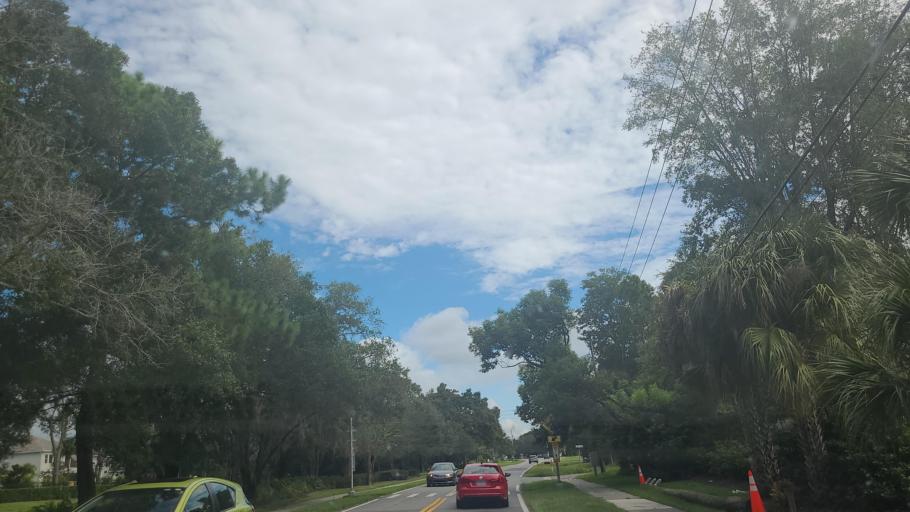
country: US
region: Florida
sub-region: Orange County
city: Lake Butler
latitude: 28.5149
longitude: -81.5422
